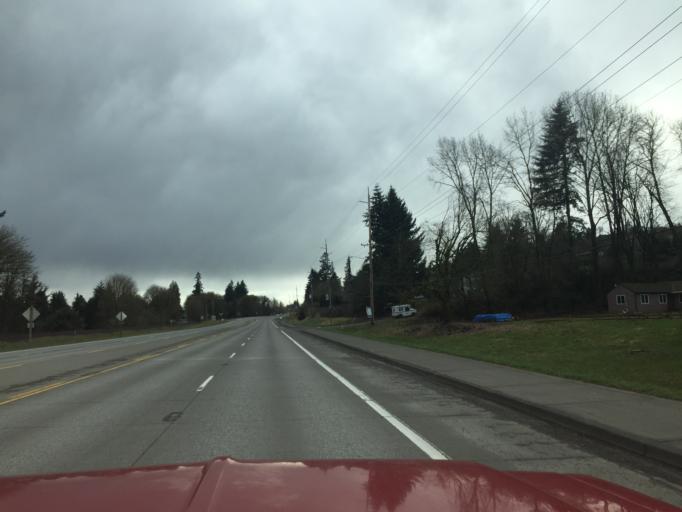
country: US
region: Oregon
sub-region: Columbia County
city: Columbia City
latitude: 45.8923
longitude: -122.8120
